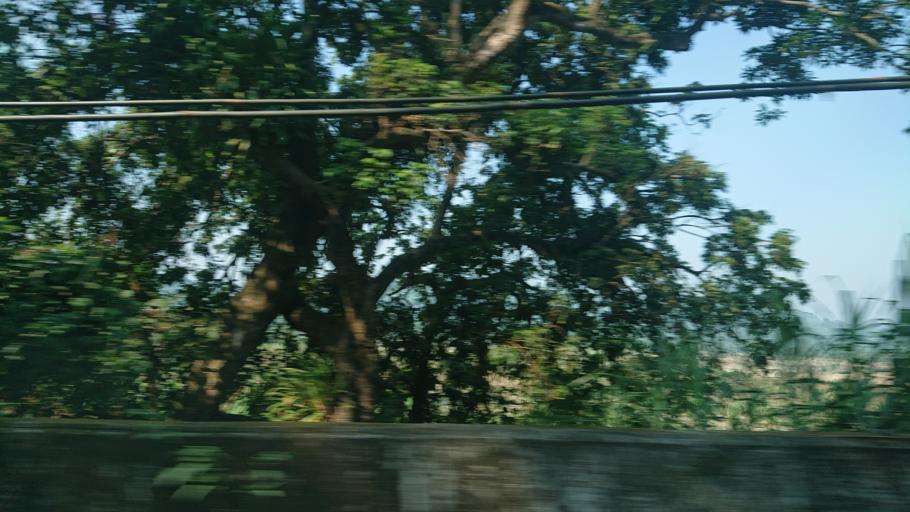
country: TW
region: Taiwan
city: Lugu
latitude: 23.7103
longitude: 120.6658
